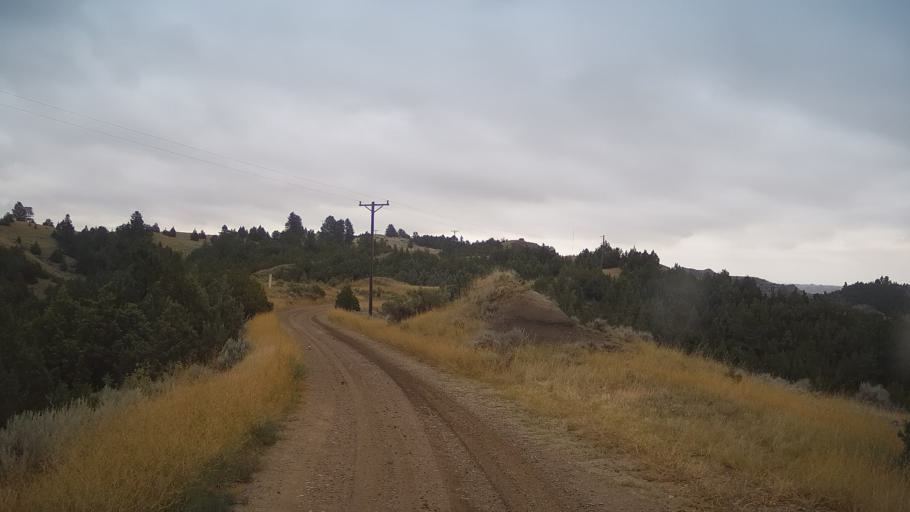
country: US
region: Montana
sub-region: Dawson County
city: Glendive
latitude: 47.0413
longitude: -104.6719
